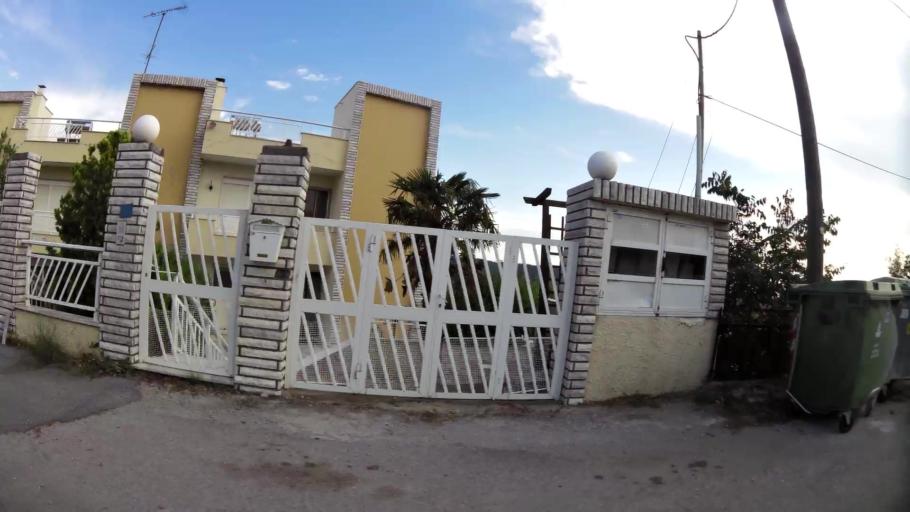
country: GR
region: Central Macedonia
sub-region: Nomos Thessalonikis
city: Pefka
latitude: 40.6584
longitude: 23.0026
